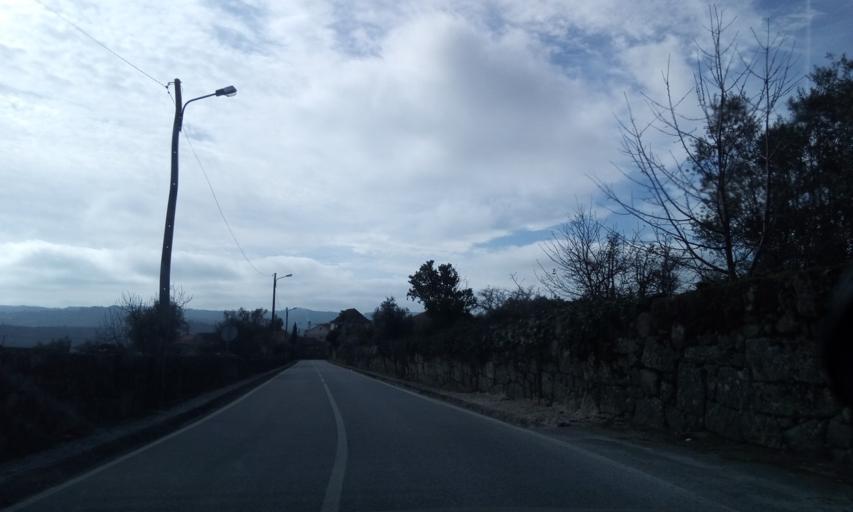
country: PT
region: Guarda
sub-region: Aguiar da Beira
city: Aguiar da Beira
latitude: 40.7348
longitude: -7.5567
